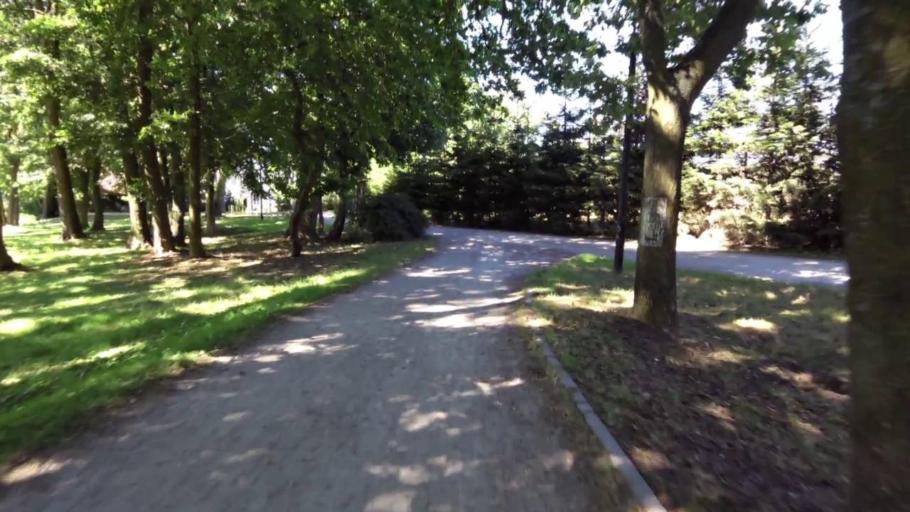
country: PL
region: West Pomeranian Voivodeship
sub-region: Powiat szczecinecki
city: Szczecinek
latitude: 53.6967
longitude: 16.6953
